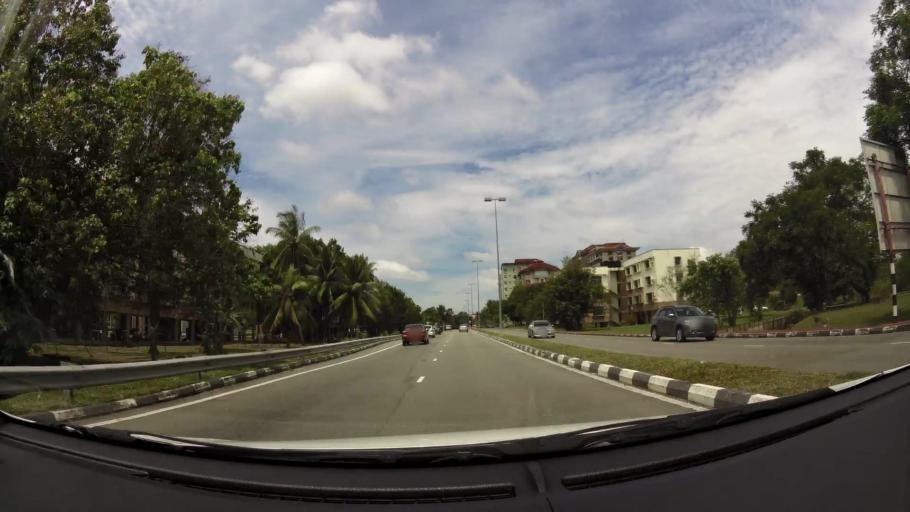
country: BN
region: Brunei and Muara
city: Bandar Seri Begawan
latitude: 4.9337
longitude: 114.9428
